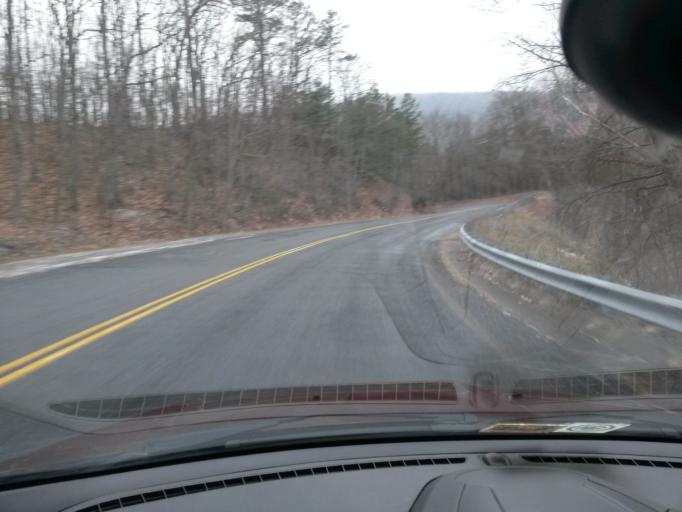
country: US
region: Virginia
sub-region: City of Lexington
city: Lexington
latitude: 37.8940
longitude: -79.5851
